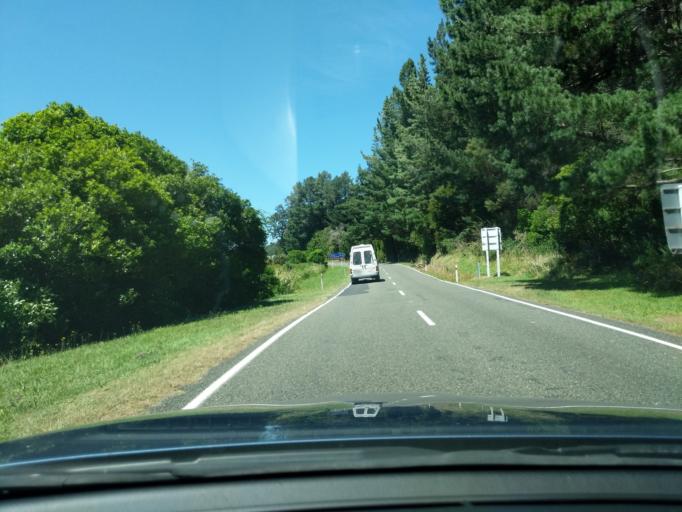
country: NZ
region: Tasman
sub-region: Tasman District
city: Takaka
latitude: -40.6822
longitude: 172.6649
